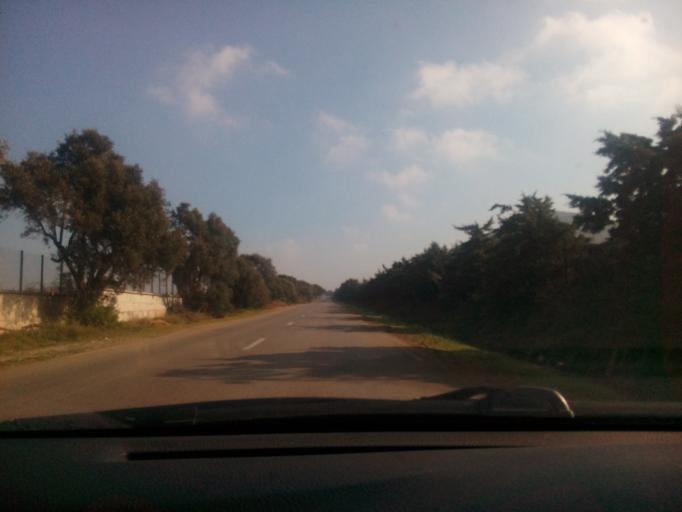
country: DZ
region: Oran
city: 'Ain el Turk
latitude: 35.7033
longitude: -0.8470
